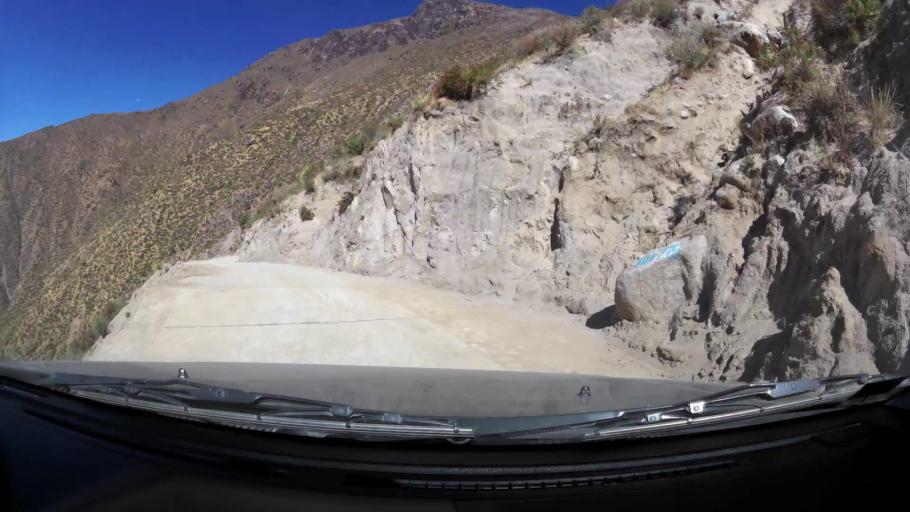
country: PE
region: Huancavelica
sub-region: Huaytara
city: Quito-Arma
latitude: -13.6171
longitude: -75.3515
